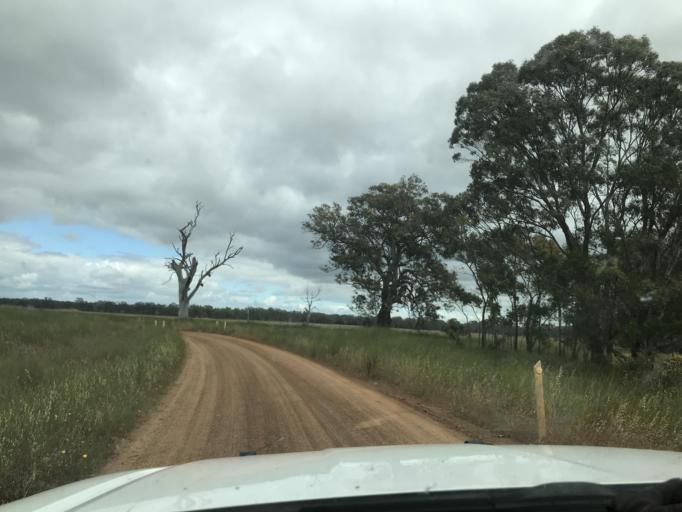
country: AU
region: South Australia
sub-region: Wattle Range
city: Penola
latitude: -37.1018
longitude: 141.2308
